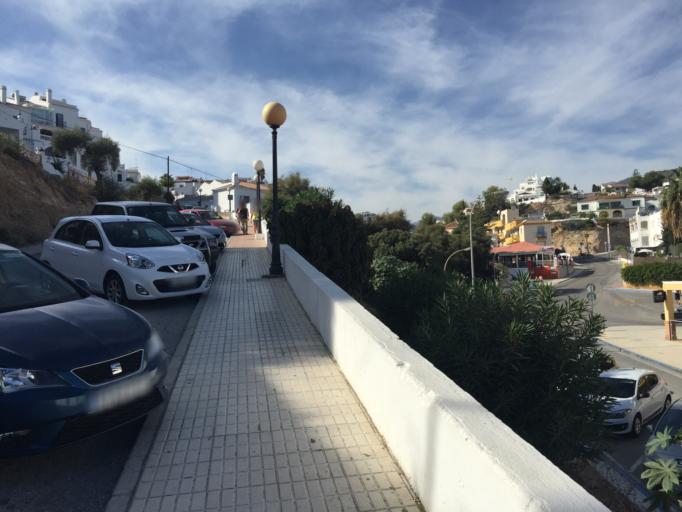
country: ES
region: Andalusia
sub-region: Provincia de Malaga
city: Nerja
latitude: 36.7505
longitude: -3.8696
